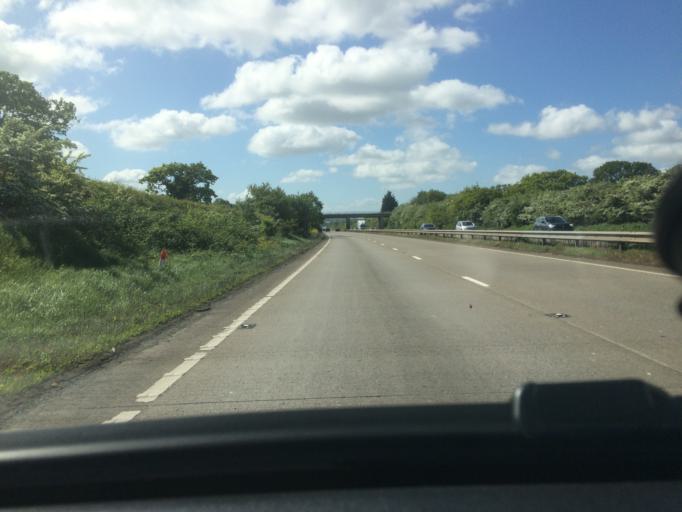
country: GB
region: Wales
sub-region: Wrexham
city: Rossett
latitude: 53.1349
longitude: -2.9461
